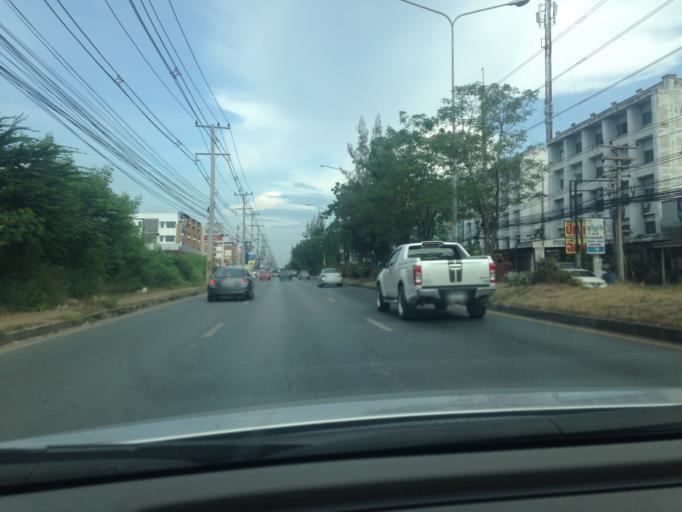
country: TH
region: Pathum Thani
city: Khlong Luang
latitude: 14.0658
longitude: 100.6554
